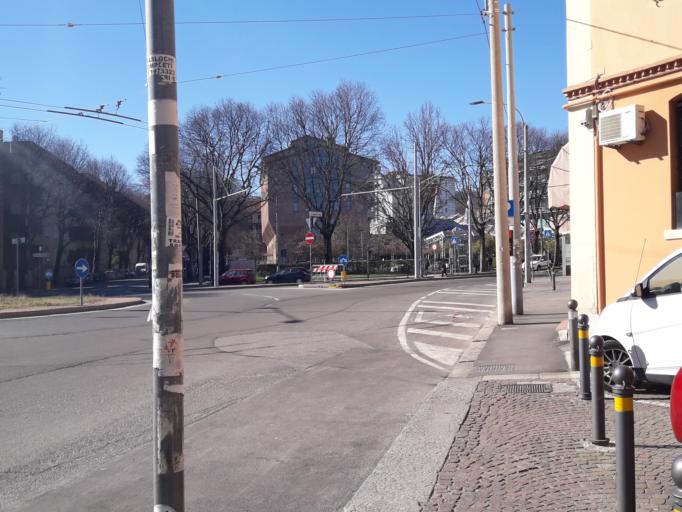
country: IT
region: Emilia-Romagna
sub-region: Provincia di Bologna
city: Bologna
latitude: 44.4949
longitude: 11.3143
